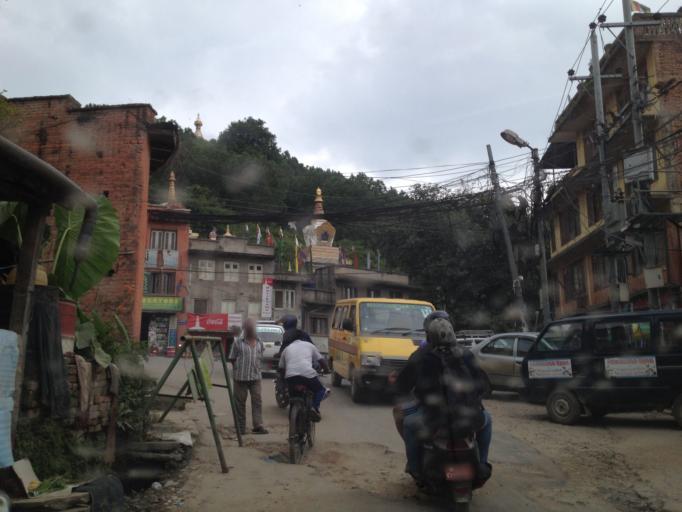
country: NP
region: Central Region
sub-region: Bagmati Zone
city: Kathmandu
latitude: 27.7127
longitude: 85.2899
